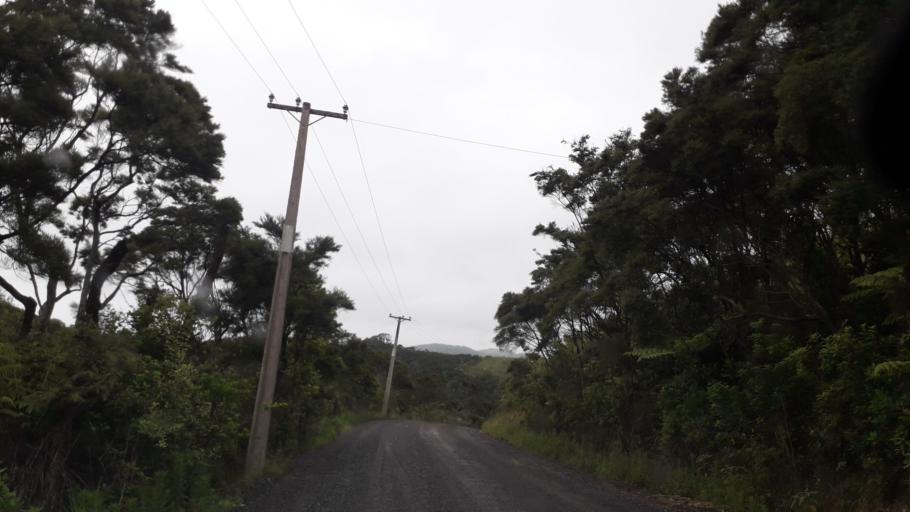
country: NZ
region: Northland
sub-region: Far North District
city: Paihia
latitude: -35.2427
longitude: 174.2482
